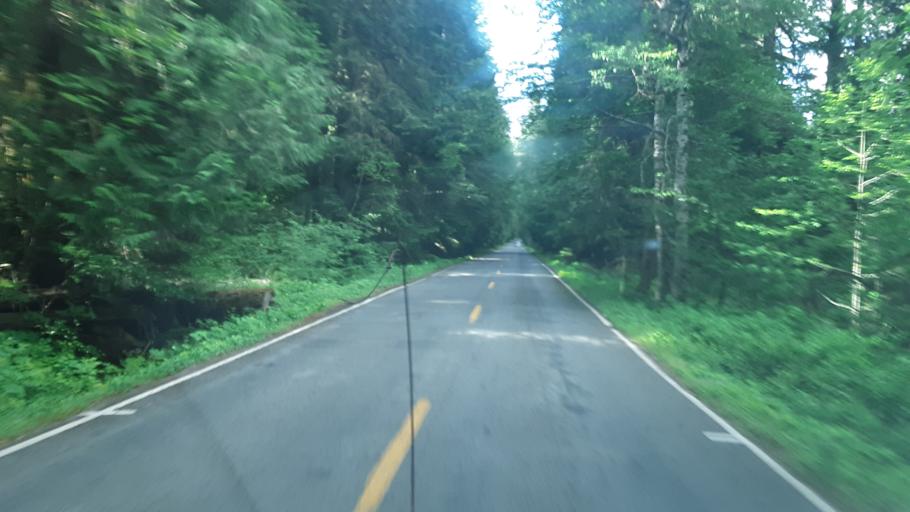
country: US
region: Washington
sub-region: Pierce County
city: Buckley
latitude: 46.7683
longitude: -121.5485
